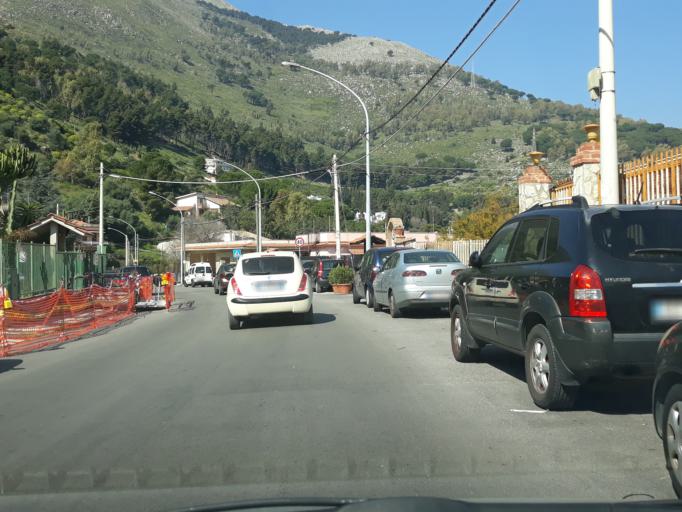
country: IT
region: Sicily
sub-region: Palermo
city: Piano dei Geli
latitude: 38.1156
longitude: 13.2921
